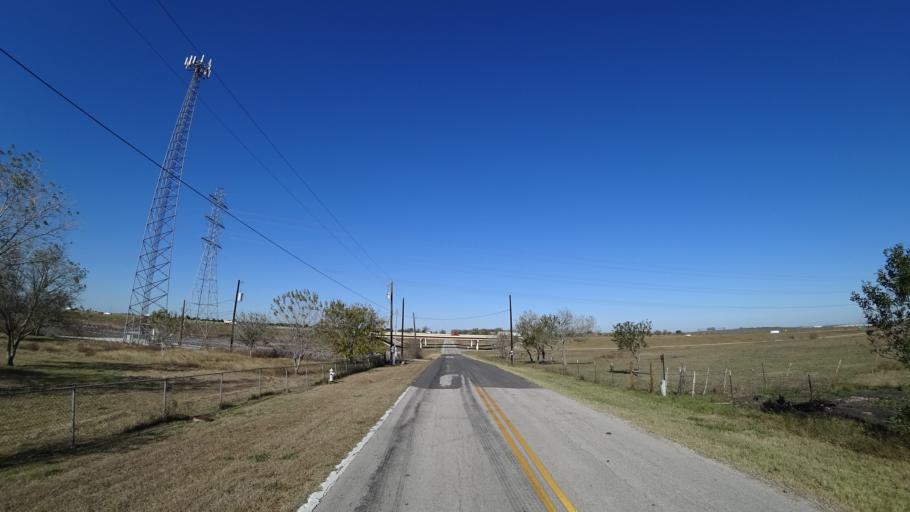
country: US
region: Texas
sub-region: Travis County
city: Onion Creek
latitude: 30.1010
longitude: -97.6672
